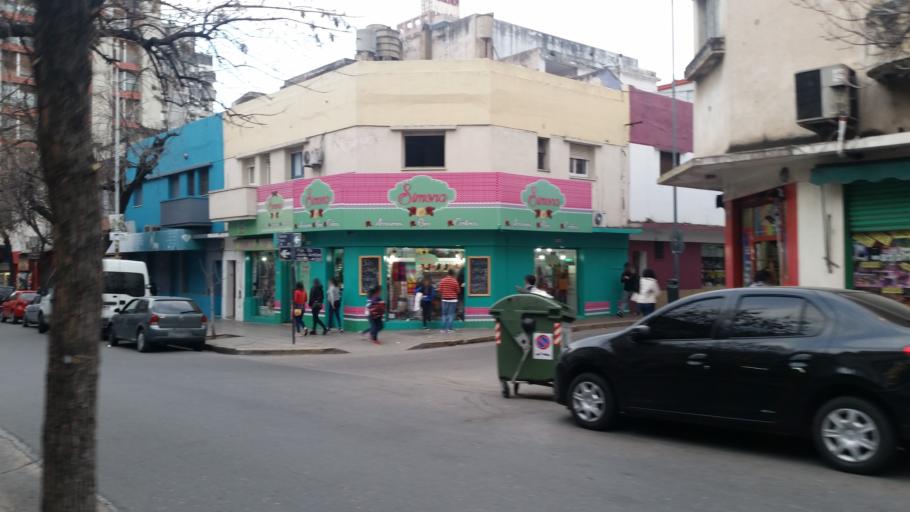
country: AR
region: Cordoba
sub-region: Departamento de Capital
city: Cordoba
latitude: -31.4208
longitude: -64.1845
